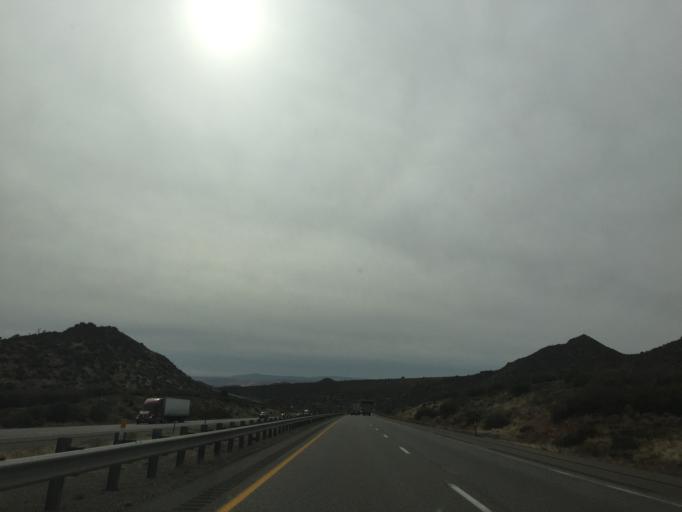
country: US
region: Utah
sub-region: Washington County
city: Toquerville
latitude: 37.3142
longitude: -113.2935
